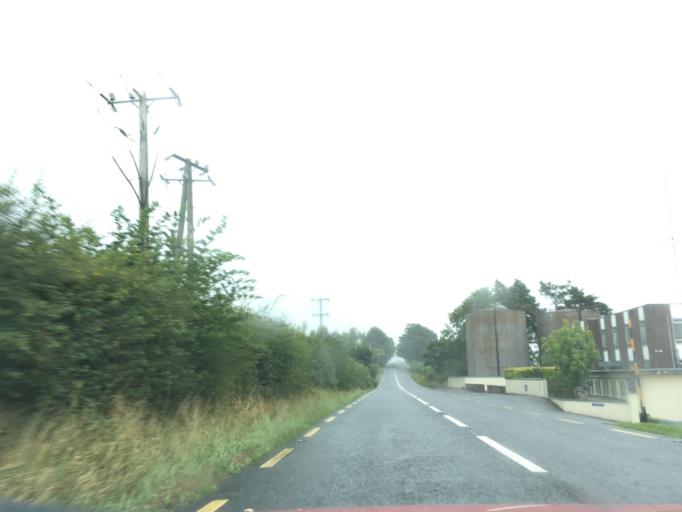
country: IE
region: Munster
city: Carrick-on-Suir
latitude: 52.3509
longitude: -7.4460
